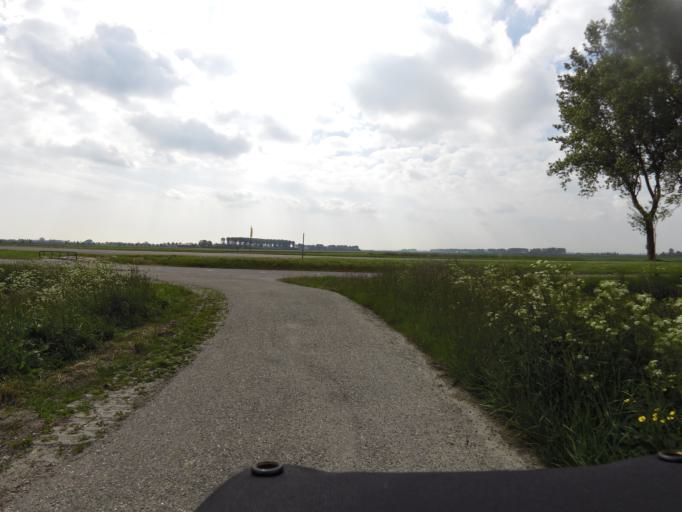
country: NL
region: Zeeland
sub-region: Gemeente Noord-Beveland
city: Kamperland
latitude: 51.5814
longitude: 3.7188
